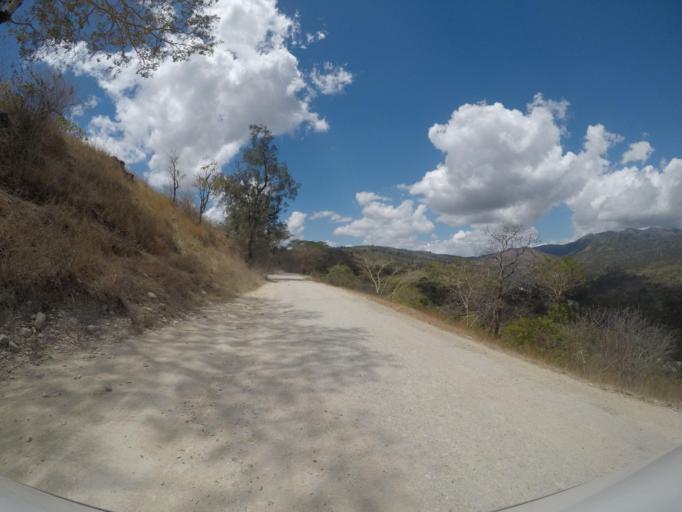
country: TL
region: Baucau
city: Baucau
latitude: -8.4855
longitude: 126.6178
